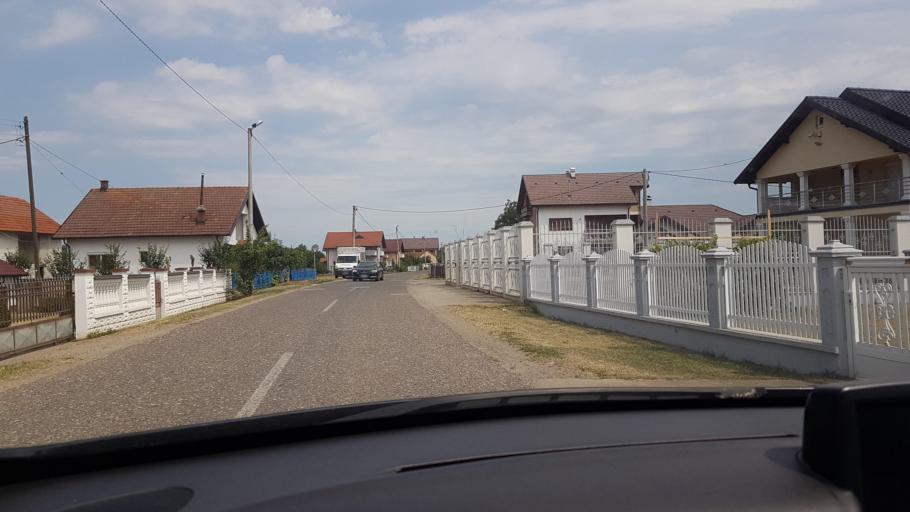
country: BA
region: Republika Srpska
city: Dvorovi
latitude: 44.8120
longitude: 19.2175
